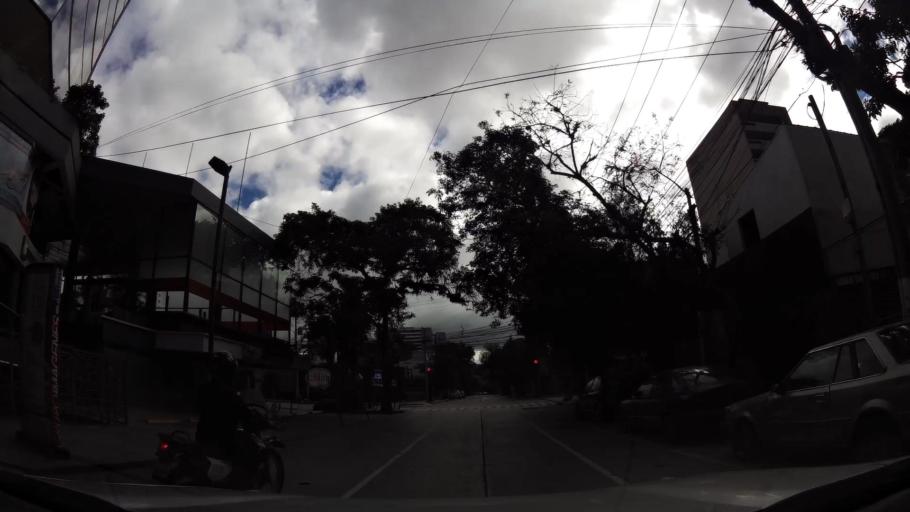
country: GT
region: Guatemala
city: Santa Catarina Pinula
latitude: 14.5978
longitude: -90.5134
